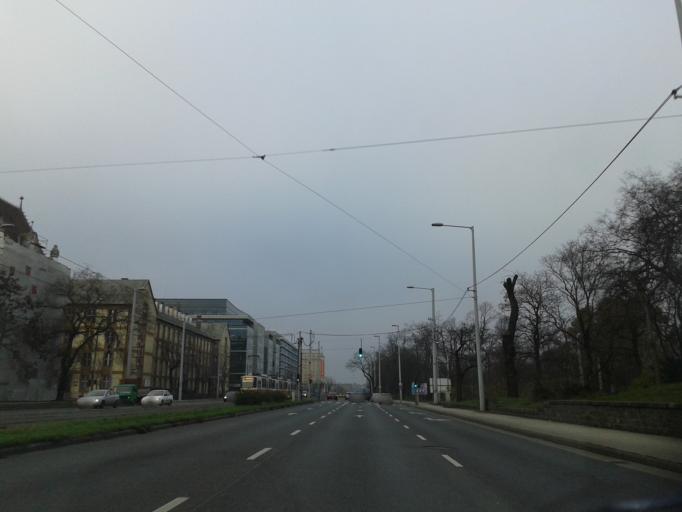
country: HU
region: Budapest
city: Budapest VIII. keruelet
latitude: 47.4776
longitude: 19.1002
